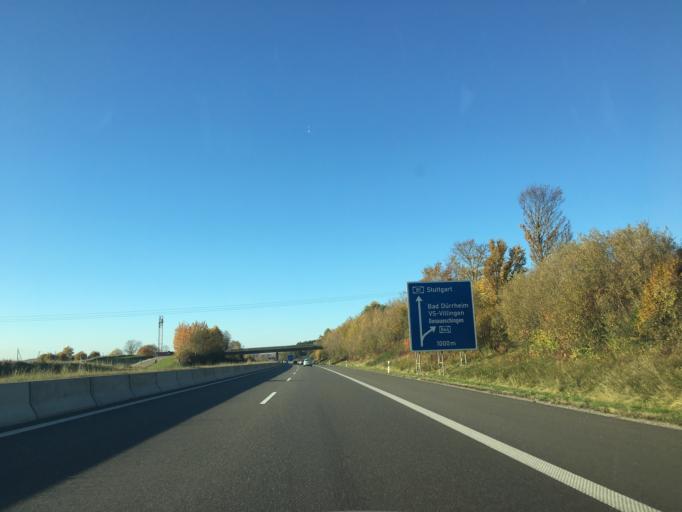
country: DE
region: Baden-Wuerttemberg
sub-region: Freiburg Region
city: Tuningen
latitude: 47.9774
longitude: 8.6176
